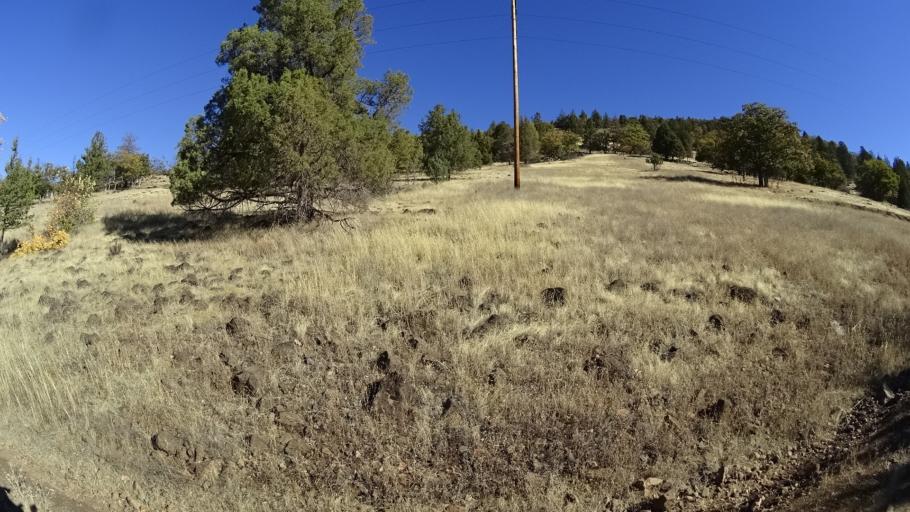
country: US
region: California
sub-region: Siskiyou County
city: Montague
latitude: 41.9766
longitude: -122.2834
